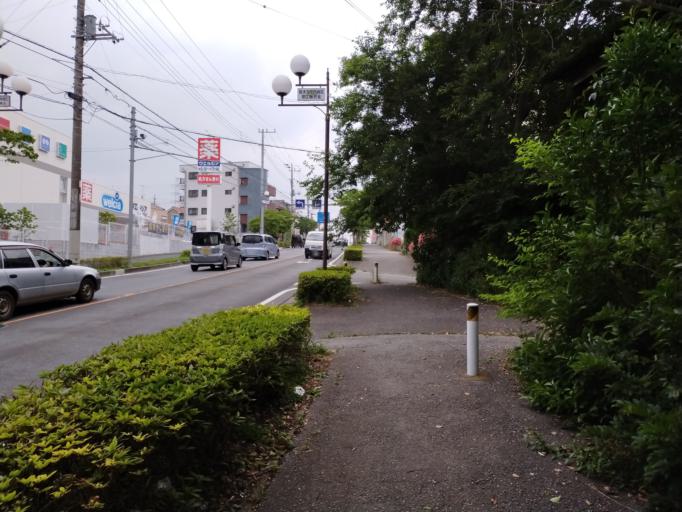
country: JP
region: Chiba
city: Yotsukaido
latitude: 35.6173
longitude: 140.1560
